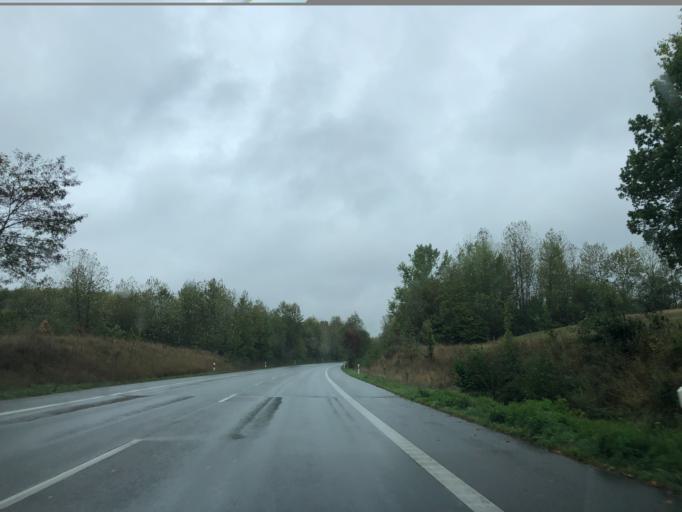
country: DE
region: North Rhine-Westphalia
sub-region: Regierungsbezirk Koln
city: Bedburg
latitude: 51.0266
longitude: 6.5795
